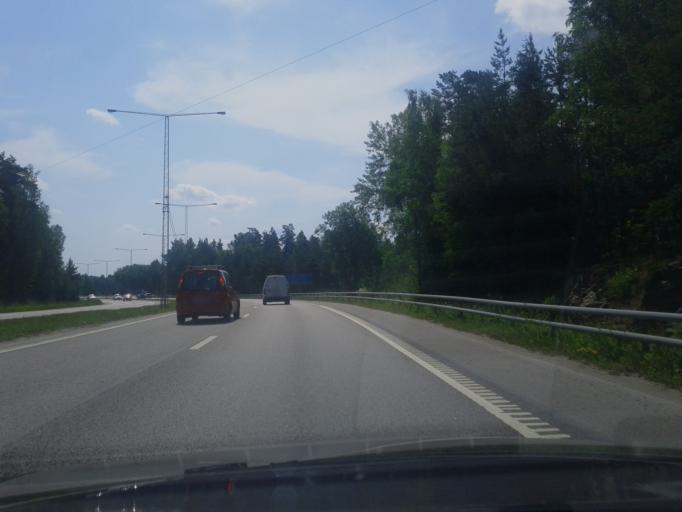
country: SE
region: Stockholm
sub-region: Taby Kommun
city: Taby
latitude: 59.4588
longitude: 18.1315
